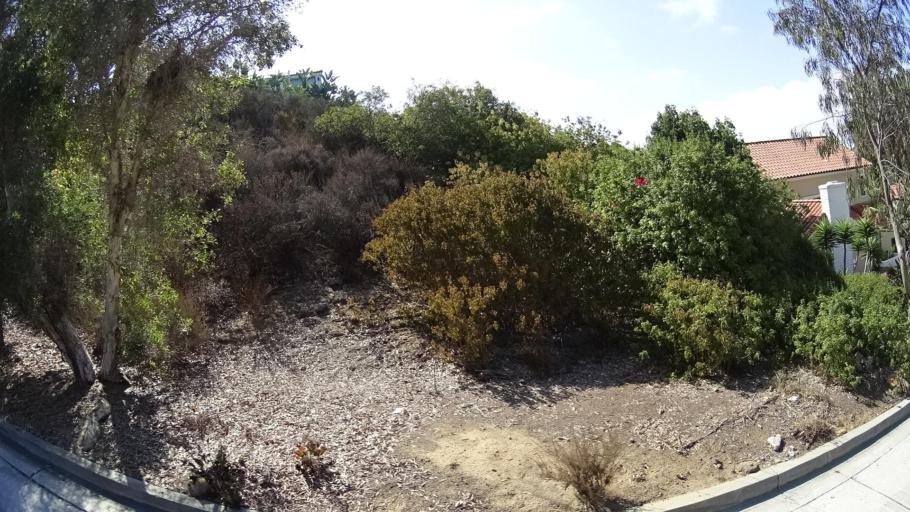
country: US
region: California
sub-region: San Diego County
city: Solana Beach
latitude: 32.9837
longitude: -117.2337
